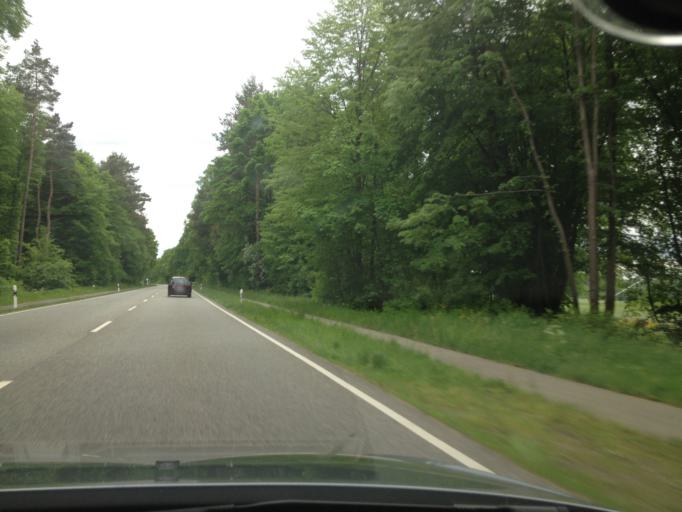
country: DE
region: Saarland
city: Kirkel
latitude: 49.2986
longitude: 7.2539
